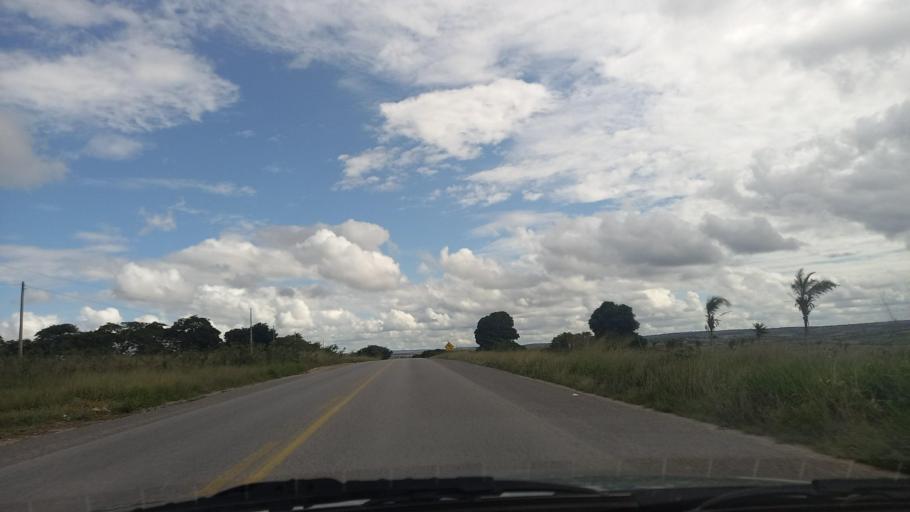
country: BR
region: Pernambuco
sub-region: Lajedo
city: Lajedo
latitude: -8.6823
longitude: -36.4065
